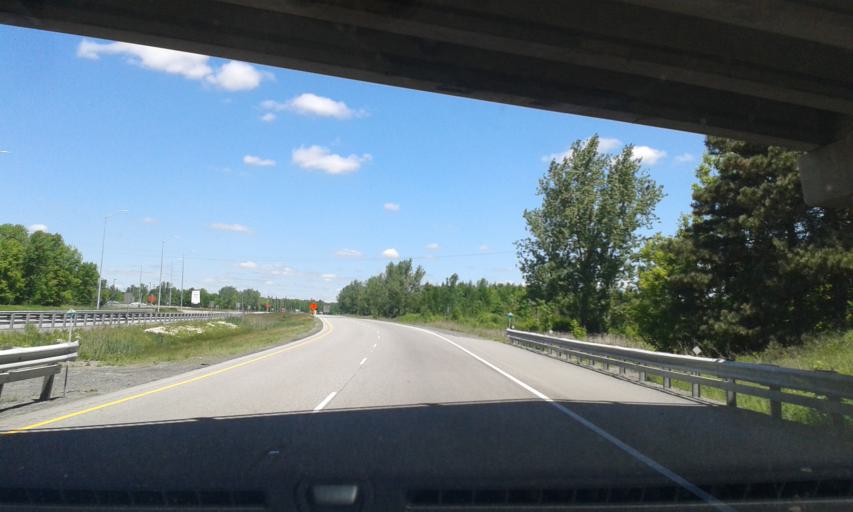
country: US
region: New York
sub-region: St. Lawrence County
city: Norfolk
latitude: 44.9668
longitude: -75.0809
